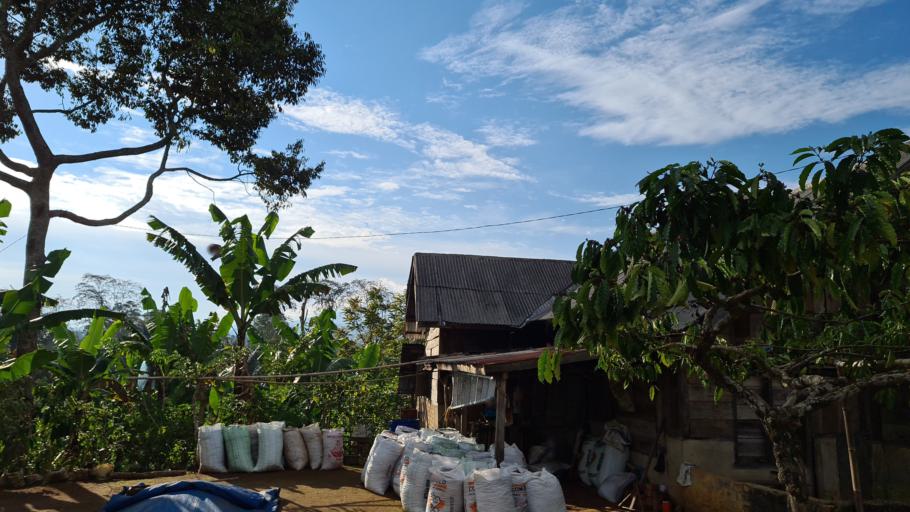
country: ID
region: Lampung
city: Kenali
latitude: -5.0804
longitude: 104.4078
